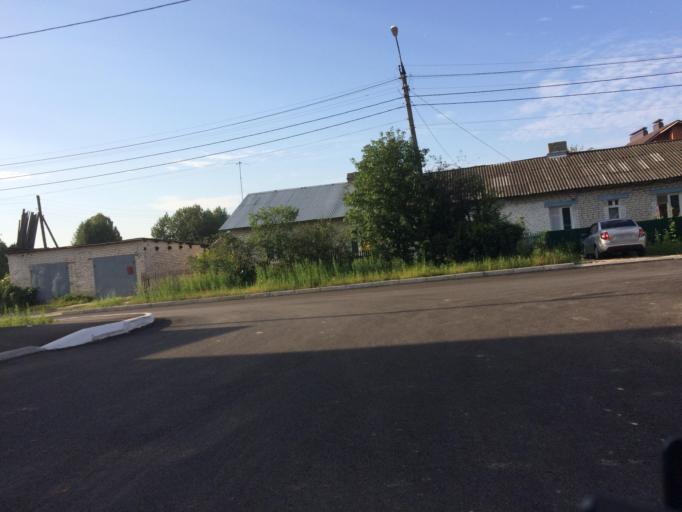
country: RU
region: Mariy-El
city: Medvedevo
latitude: 56.6352
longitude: 47.8115
